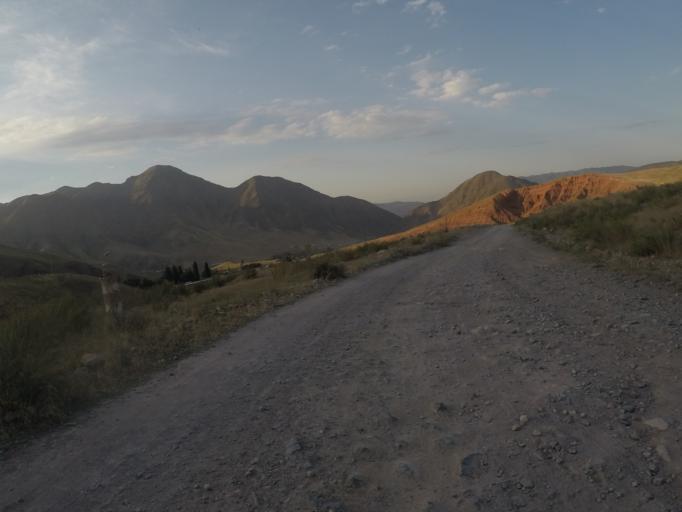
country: KG
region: Chuy
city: Bishkek
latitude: 42.6591
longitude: 74.6506
